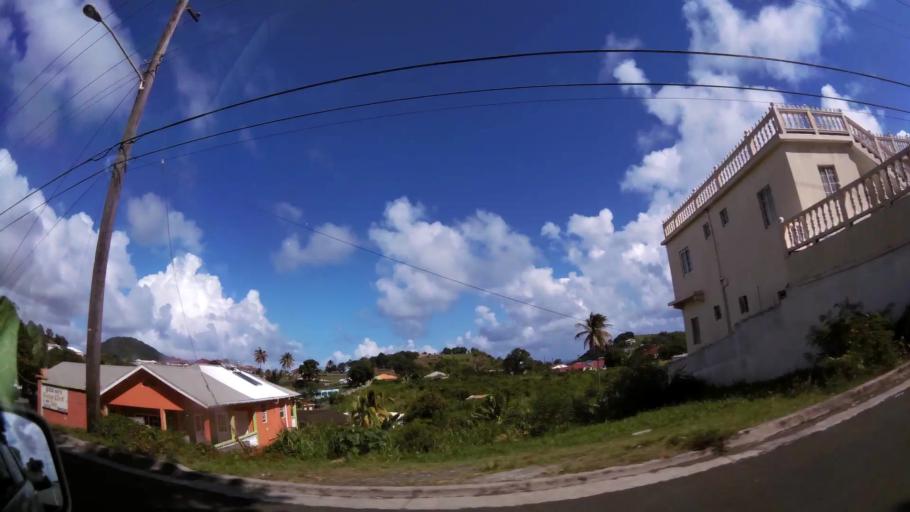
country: VC
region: Saint George
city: Kingstown
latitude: 13.1356
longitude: -61.1789
